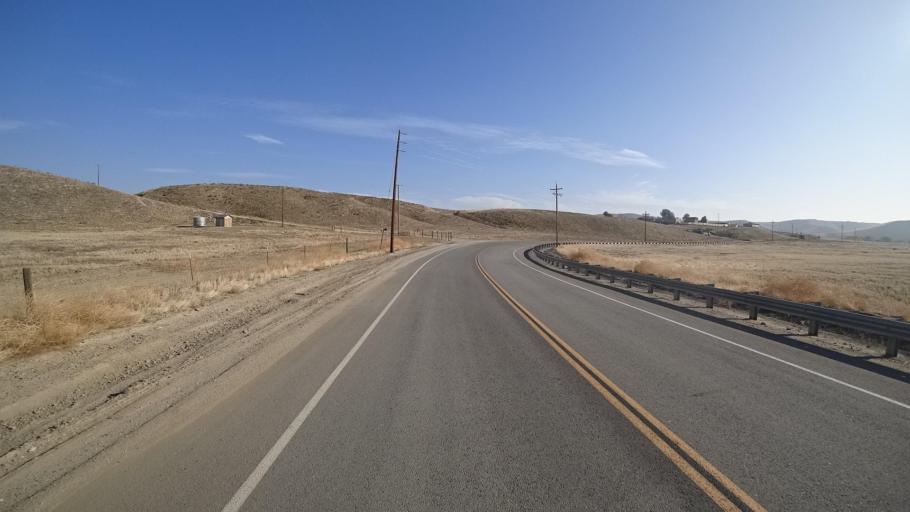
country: US
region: California
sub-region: Kern County
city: Oildale
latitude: 35.4446
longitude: -118.8963
